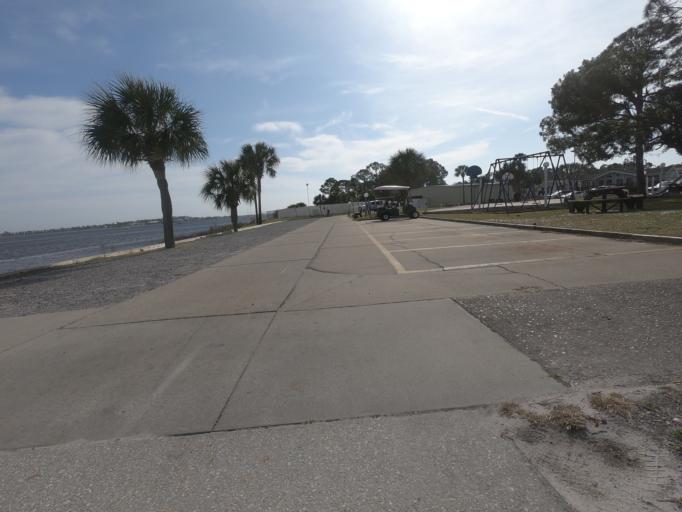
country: US
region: Florida
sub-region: Bay County
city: Lower Grand Lagoon
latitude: 30.1420
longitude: -85.7454
